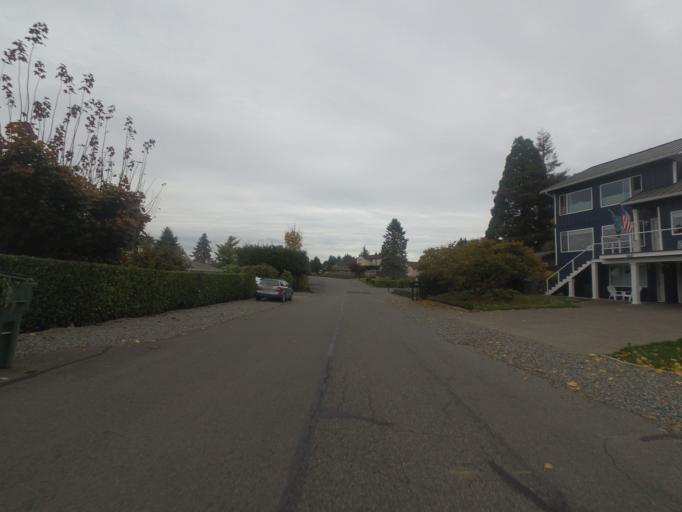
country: US
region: Washington
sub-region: Pierce County
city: University Place
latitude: 47.2217
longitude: -122.5648
